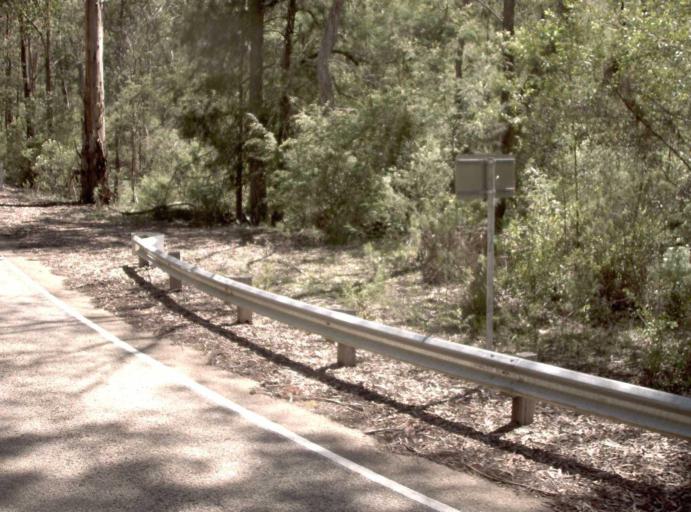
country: AU
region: Victoria
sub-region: East Gippsland
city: Lakes Entrance
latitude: -37.3687
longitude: 148.2187
